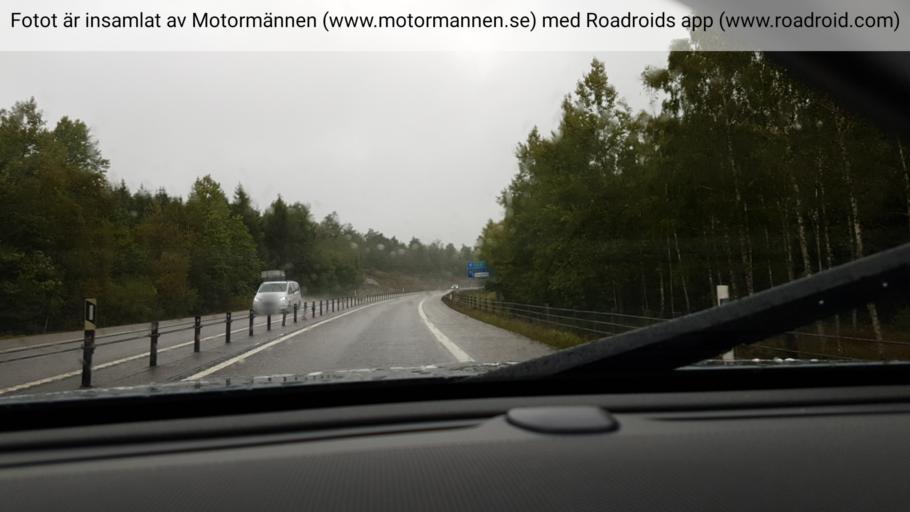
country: SE
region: Vaestra Goetaland
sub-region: Vanersborgs Kommun
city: Vanersborg
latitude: 58.3779
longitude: 12.2779
